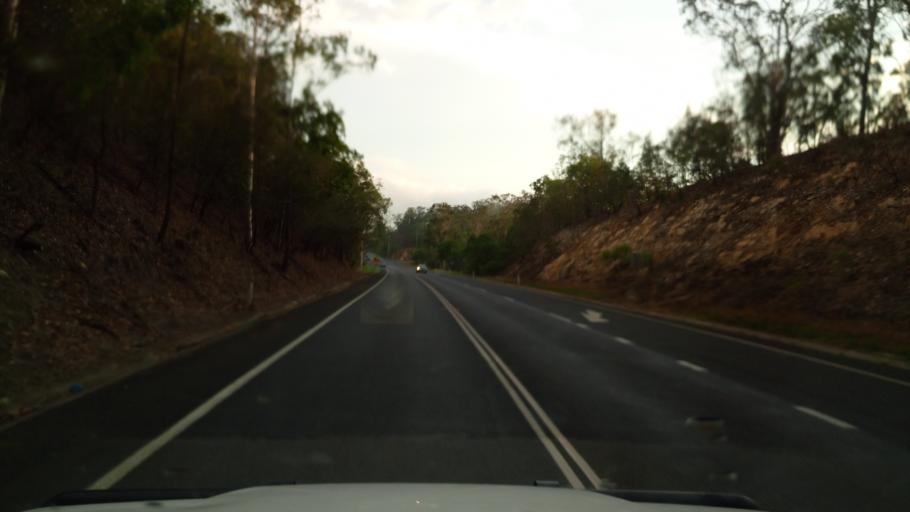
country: AU
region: Queensland
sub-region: Tablelands
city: Kuranda
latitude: -16.8516
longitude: 145.6012
